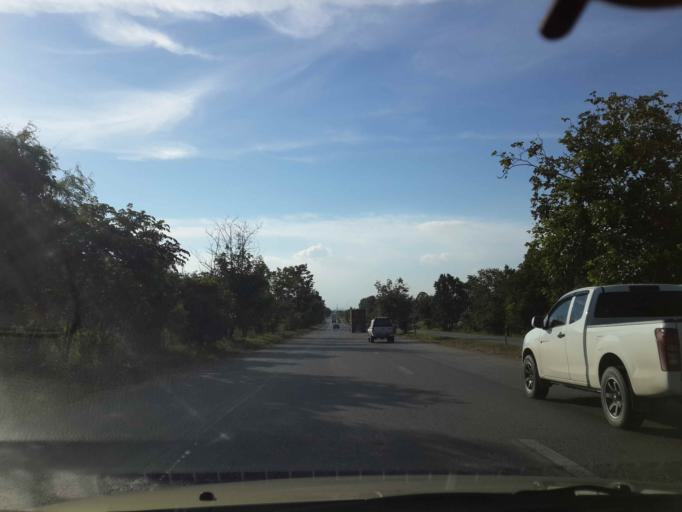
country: TH
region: Chon Buri
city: Phatthaya
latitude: 12.9350
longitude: 100.9985
